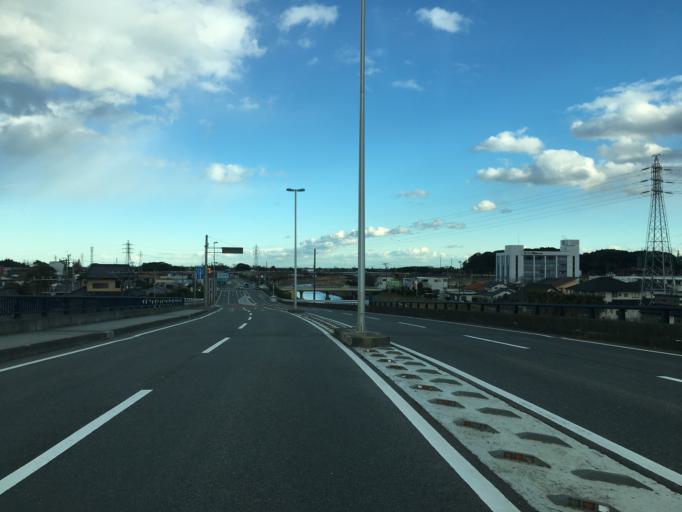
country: JP
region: Ibaraki
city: Kitaibaraki
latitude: 36.8964
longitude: 140.7800
